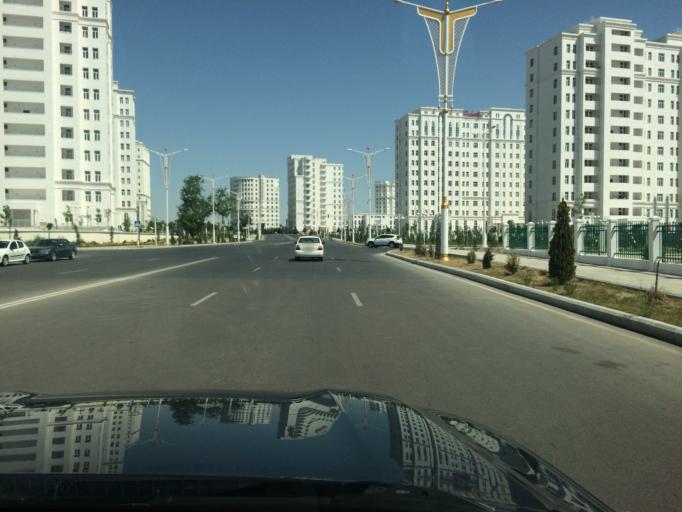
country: TM
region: Ahal
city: Ashgabat
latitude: 37.9167
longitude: 58.3615
